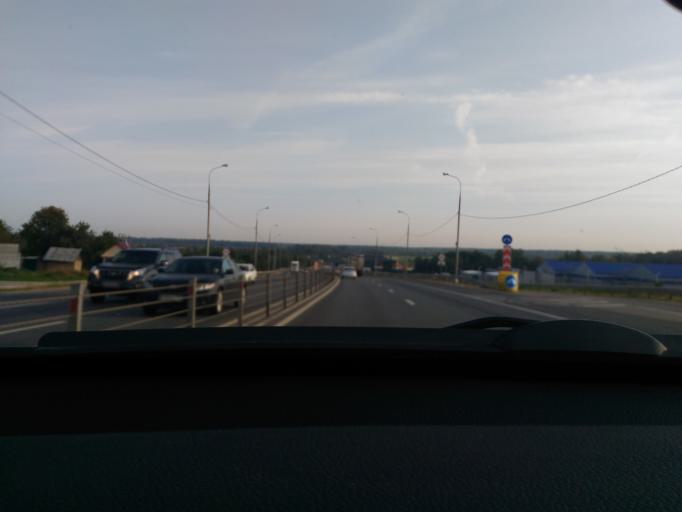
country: RU
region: Moskovskaya
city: Nekrasovskiy
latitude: 56.0737
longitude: 37.5196
